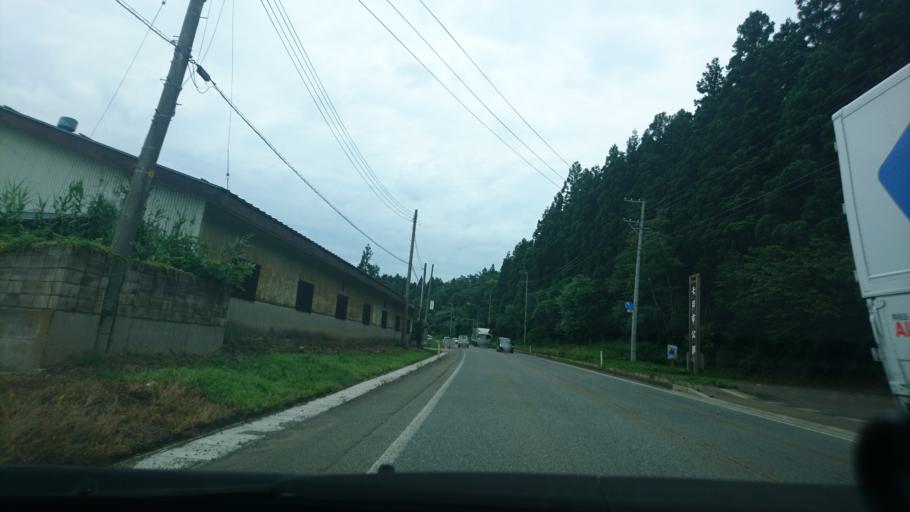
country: JP
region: Akita
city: Yokotemachi
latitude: 39.3355
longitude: 140.5603
